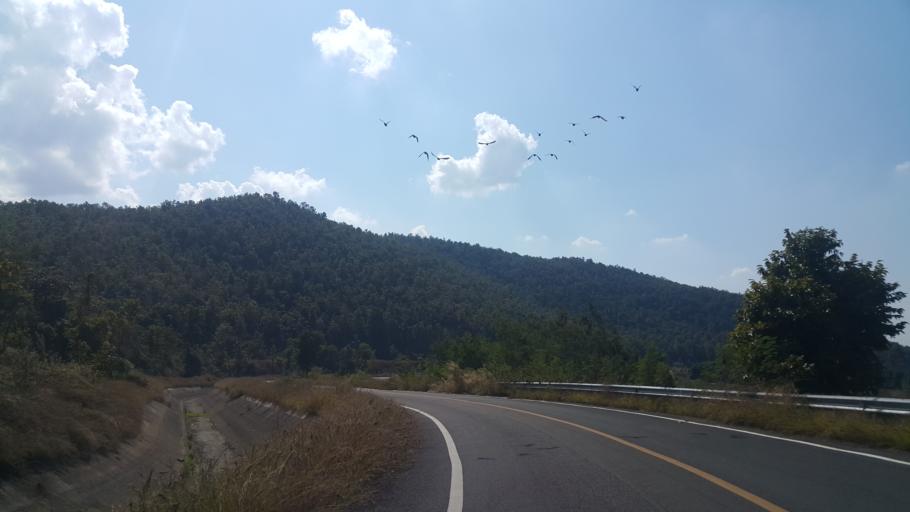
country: TH
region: Lamphun
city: Ban Thi
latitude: 18.6295
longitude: 99.1472
